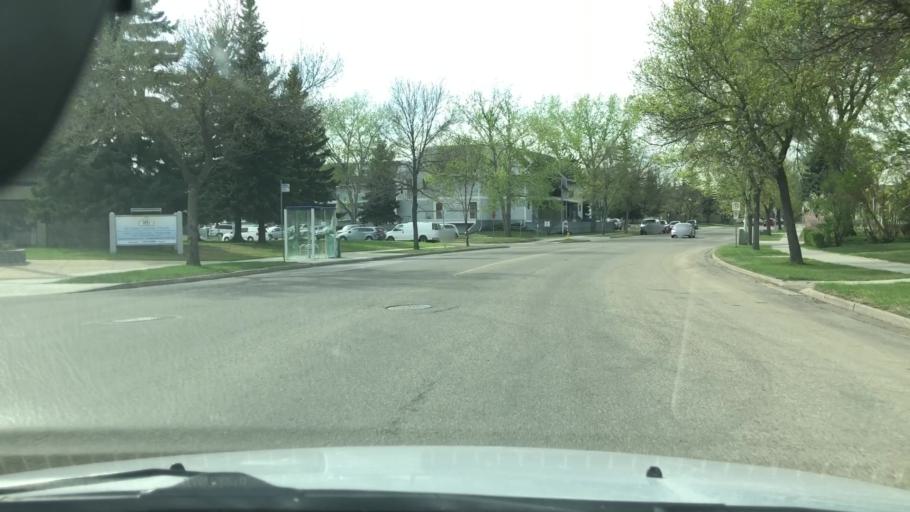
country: CA
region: Alberta
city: Edmonton
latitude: 53.6013
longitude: -113.5276
